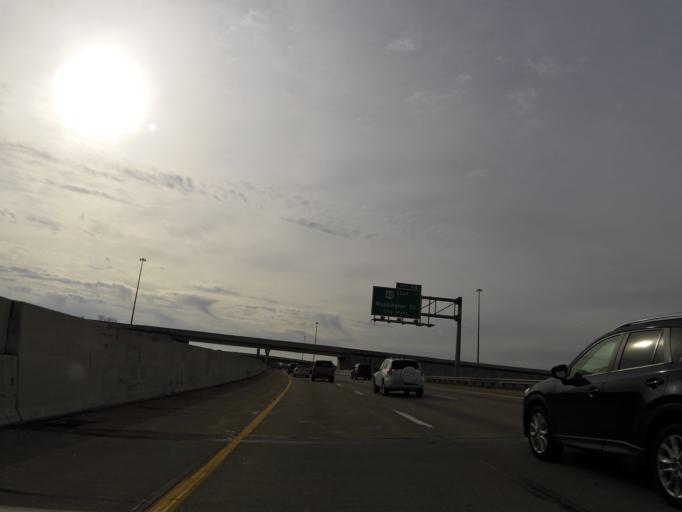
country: US
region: Indiana
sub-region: Marion County
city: Warren Park
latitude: 39.7988
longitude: -86.0350
